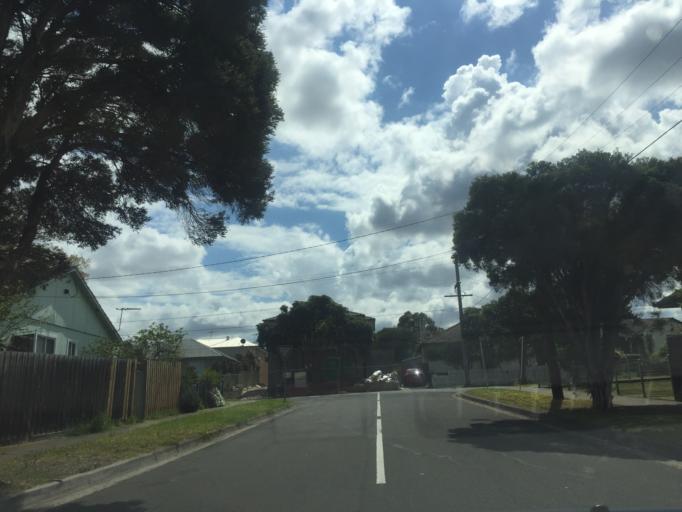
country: AU
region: Victoria
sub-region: Darebin
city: Kingsbury
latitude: -37.7290
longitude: 145.0322
